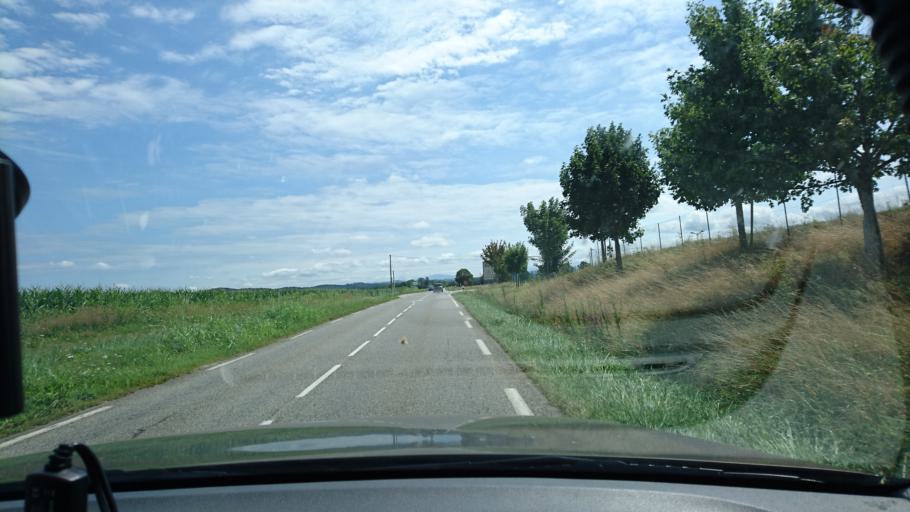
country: FR
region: Midi-Pyrenees
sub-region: Departement de la Haute-Garonne
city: Gaillac-Toulza
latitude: 43.1664
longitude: 1.4156
